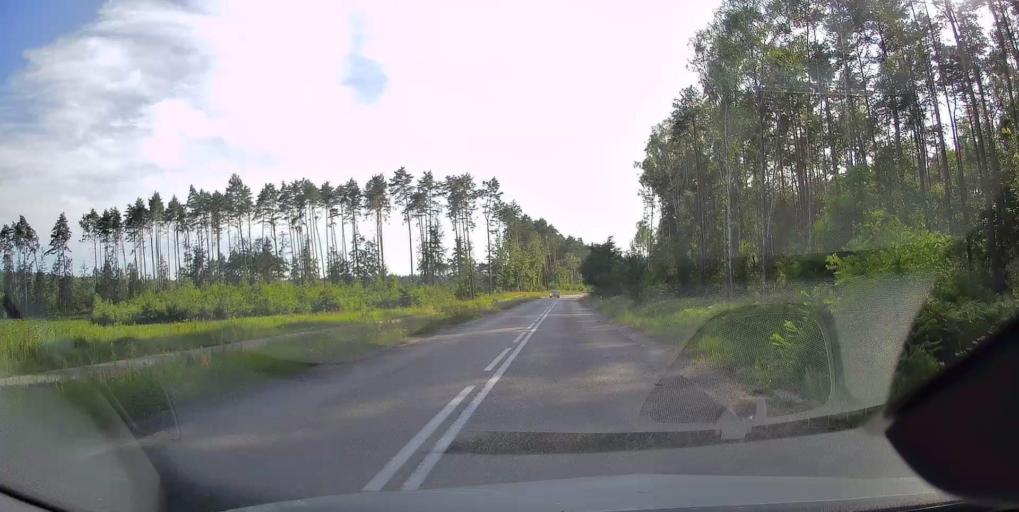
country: PL
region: Swietokrzyskie
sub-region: Powiat konecki
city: Radoszyce
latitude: 51.0976
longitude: 20.3090
